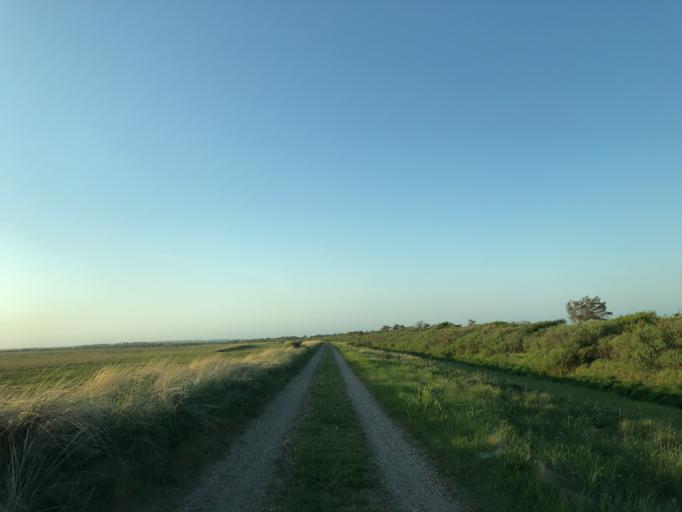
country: DK
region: Central Jutland
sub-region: Holstebro Kommune
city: Ulfborg
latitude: 56.2327
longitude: 8.1667
